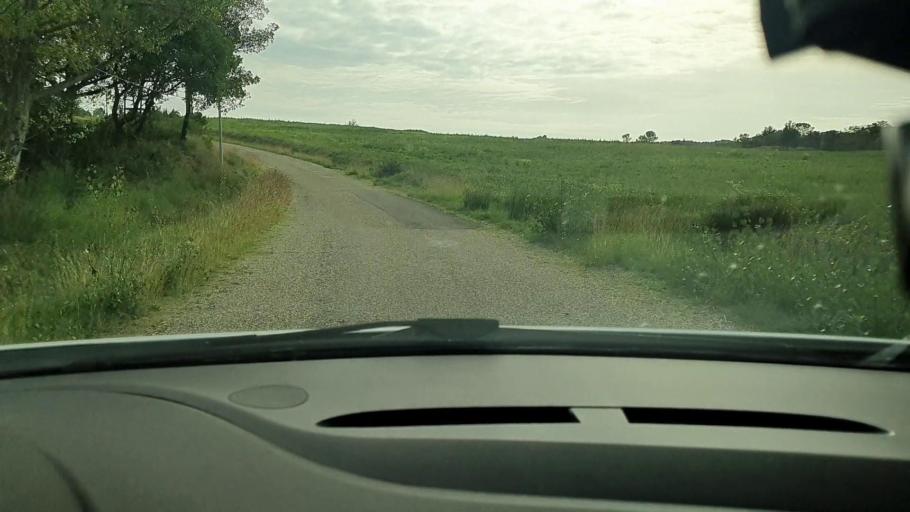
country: FR
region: Languedoc-Roussillon
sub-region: Departement du Gard
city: Montaren-et-Saint-Mediers
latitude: 44.0900
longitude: 4.3381
